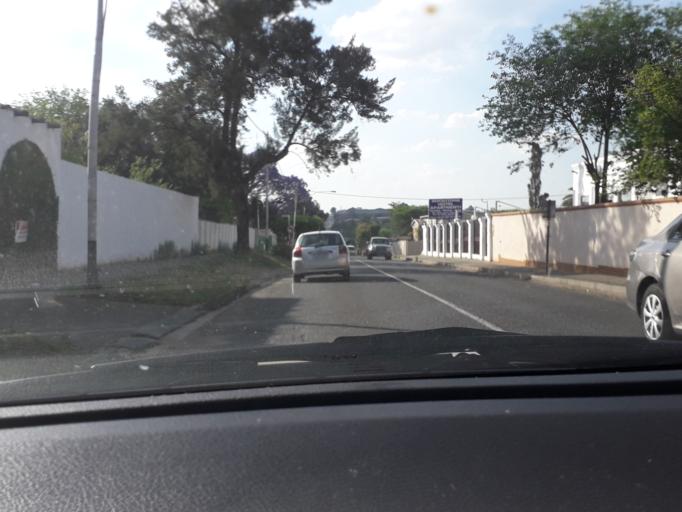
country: ZA
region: Gauteng
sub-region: City of Johannesburg Metropolitan Municipality
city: Modderfontein
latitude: -26.1287
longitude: 28.0972
